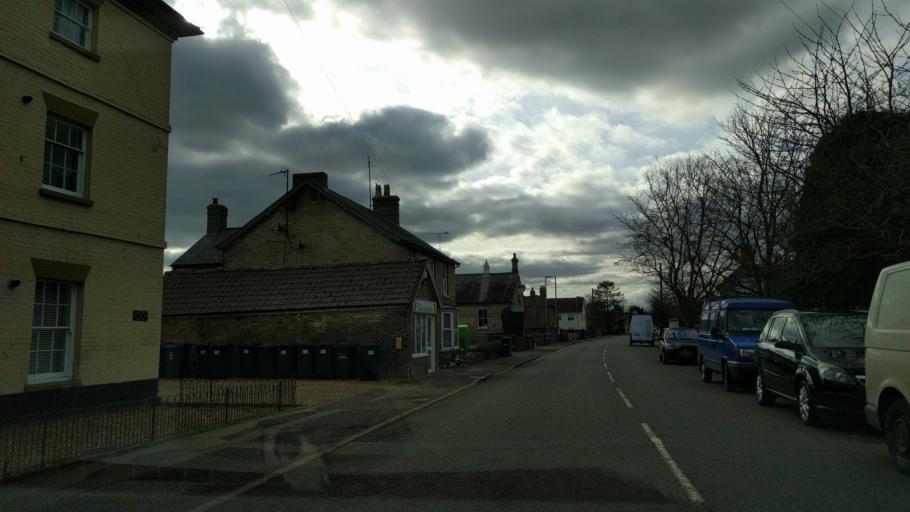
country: GB
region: England
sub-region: Cambridgeshire
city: Warboys
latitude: 52.4035
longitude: -0.0789
